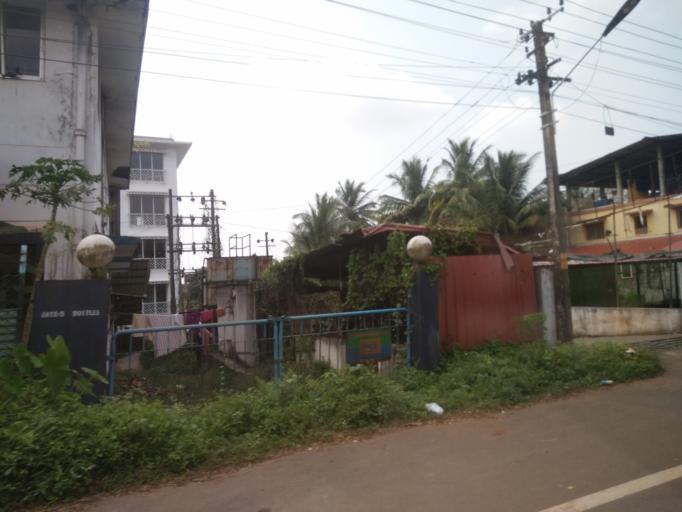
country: IN
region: Goa
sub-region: North Goa
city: Panaji
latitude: 15.5202
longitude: 73.8285
